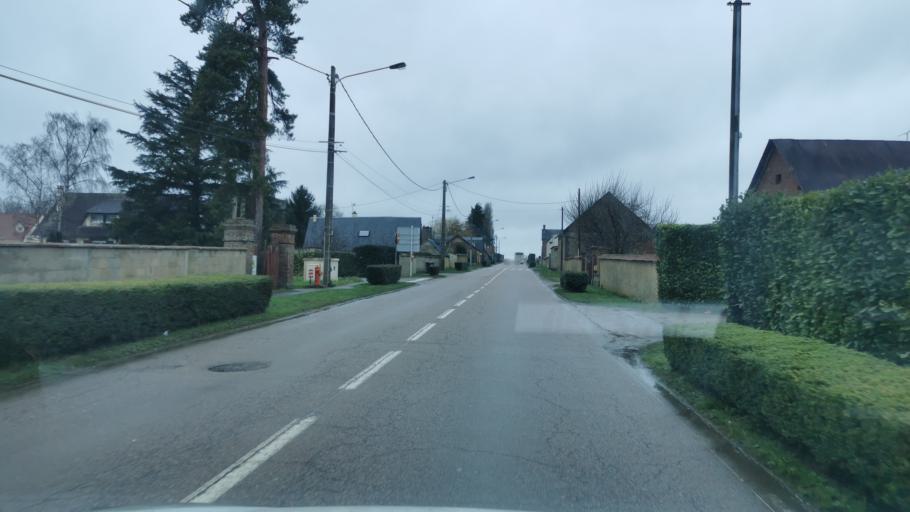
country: FR
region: Haute-Normandie
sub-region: Departement de l'Eure
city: Normanville
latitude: 49.0834
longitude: 1.1811
